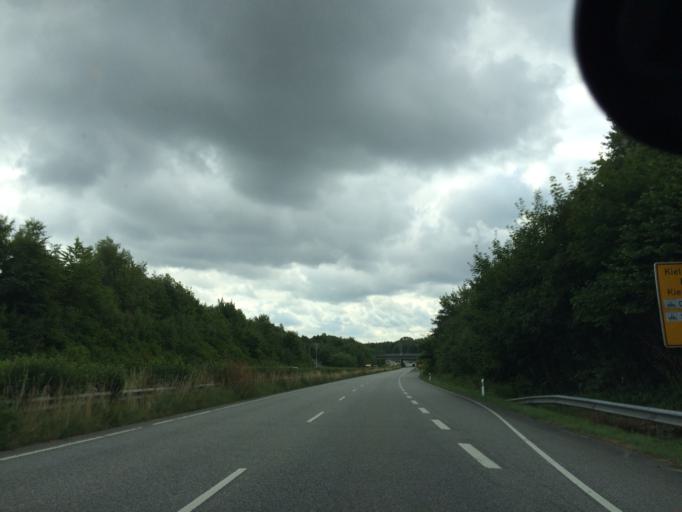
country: DE
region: Schleswig-Holstein
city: Kronshagen
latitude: 54.3602
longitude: 10.0909
